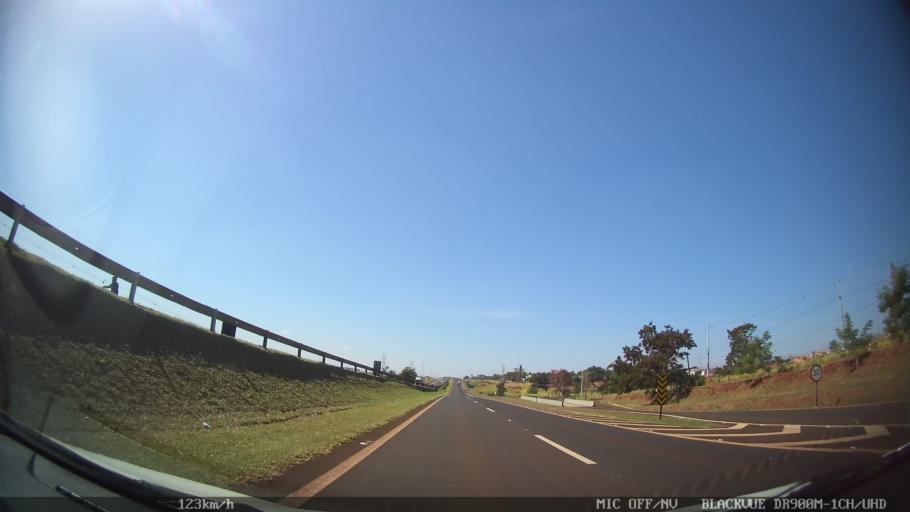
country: BR
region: Sao Paulo
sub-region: Ribeirao Preto
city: Ribeirao Preto
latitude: -21.1378
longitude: -47.8631
